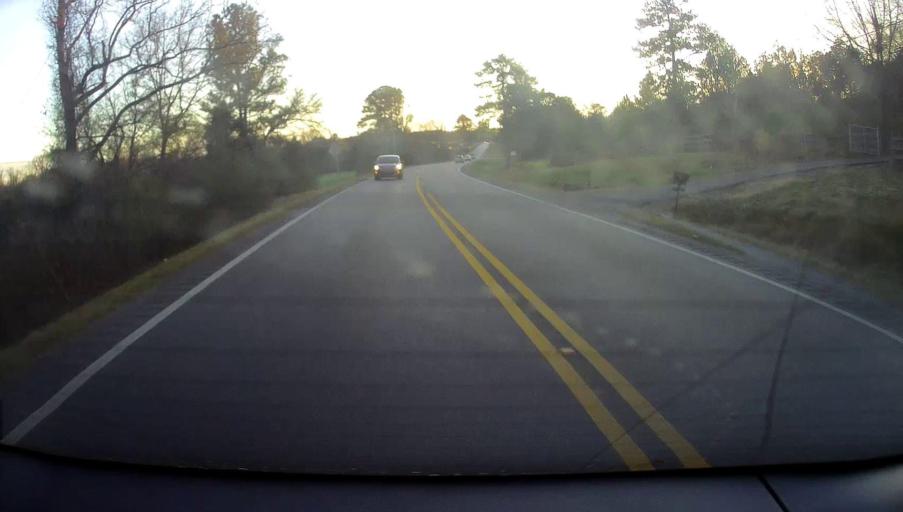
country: US
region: Alabama
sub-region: Etowah County
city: Attalla
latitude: 34.0185
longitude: -86.1177
